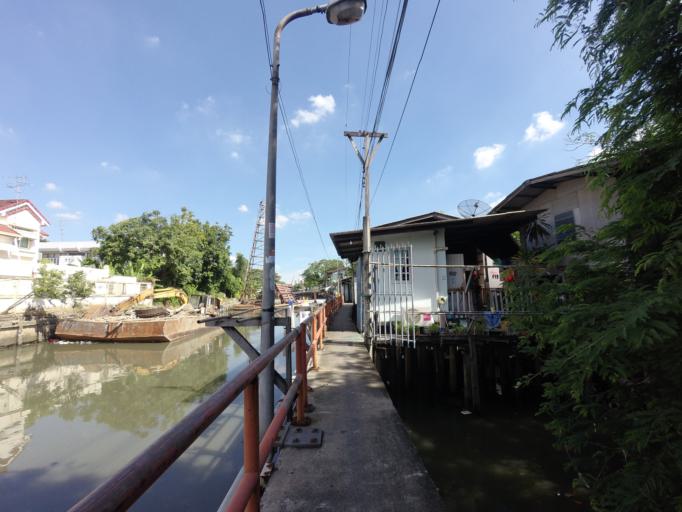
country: TH
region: Bangkok
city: Huai Khwang
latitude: 13.7922
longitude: 100.5893
